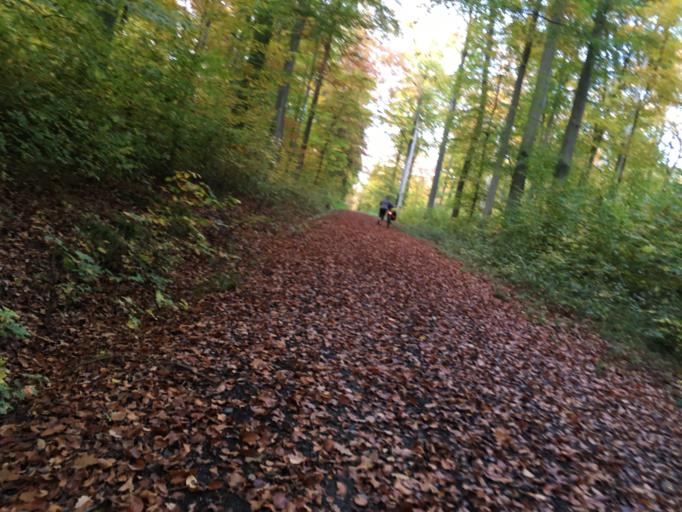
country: DE
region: Baden-Wuerttemberg
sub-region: Regierungsbezirk Stuttgart
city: Ittlingen
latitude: 49.2345
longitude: 8.9491
